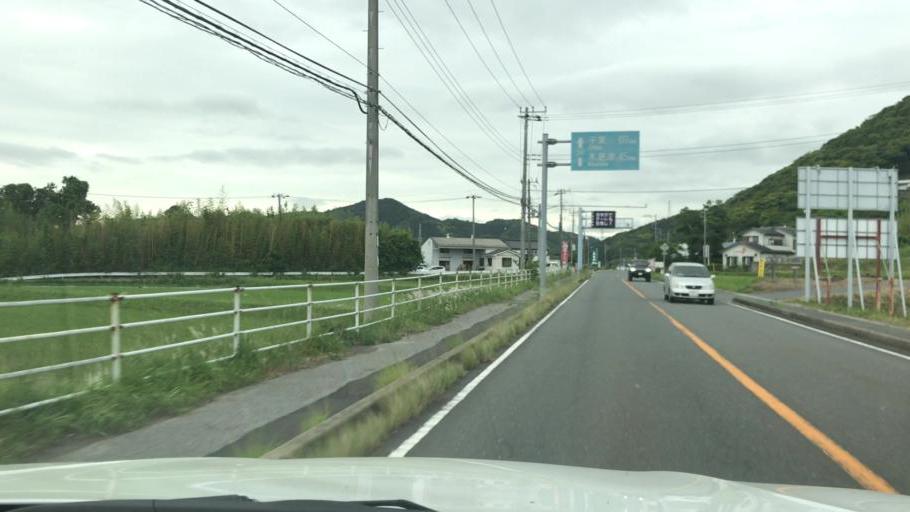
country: JP
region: Chiba
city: Kawaguchi
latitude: 35.1240
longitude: 140.0813
